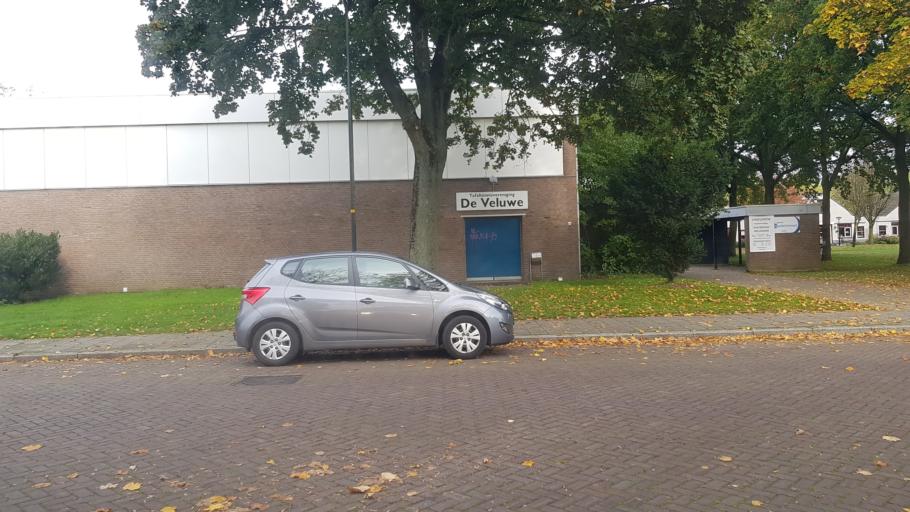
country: NL
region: Gelderland
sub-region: Gemeente Apeldoorn
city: Apeldoorn
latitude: 52.2330
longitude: 5.9632
